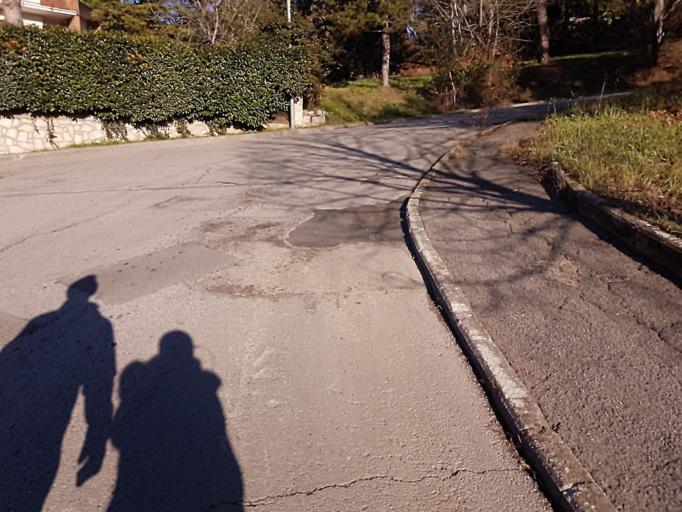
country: IT
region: Umbria
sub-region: Provincia di Perugia
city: Perugia
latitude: 43.0961
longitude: 12.3721
